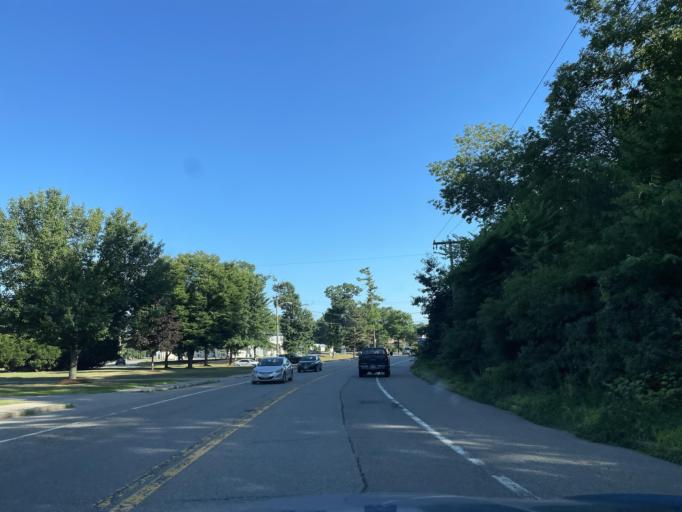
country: US
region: Massachusetts
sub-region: Norfolk County
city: Foxborough
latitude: 42.0563
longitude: -71.2420
